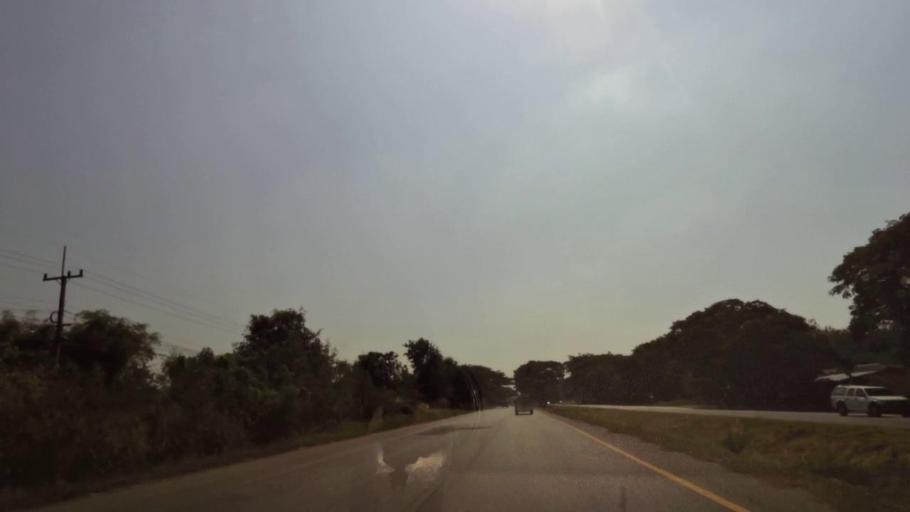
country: TH
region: Phichit
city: Bueng Na Rang
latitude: 16.3402
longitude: 100.1283
